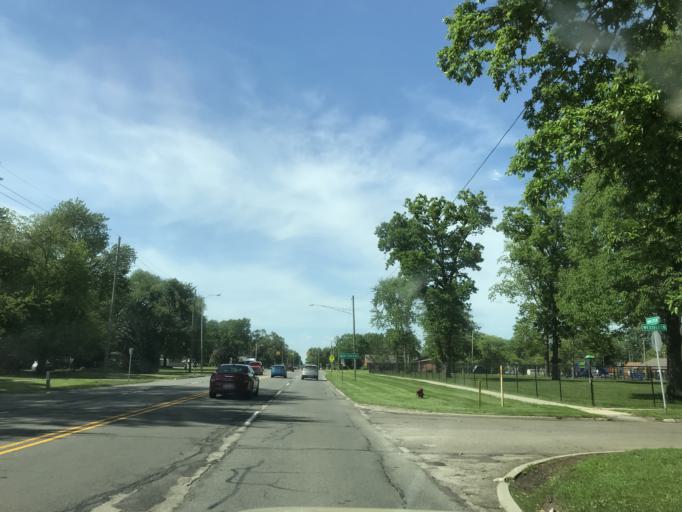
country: US
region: Michigan
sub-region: Wayne County
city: Redford
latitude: 42.3606
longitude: -83.3130
